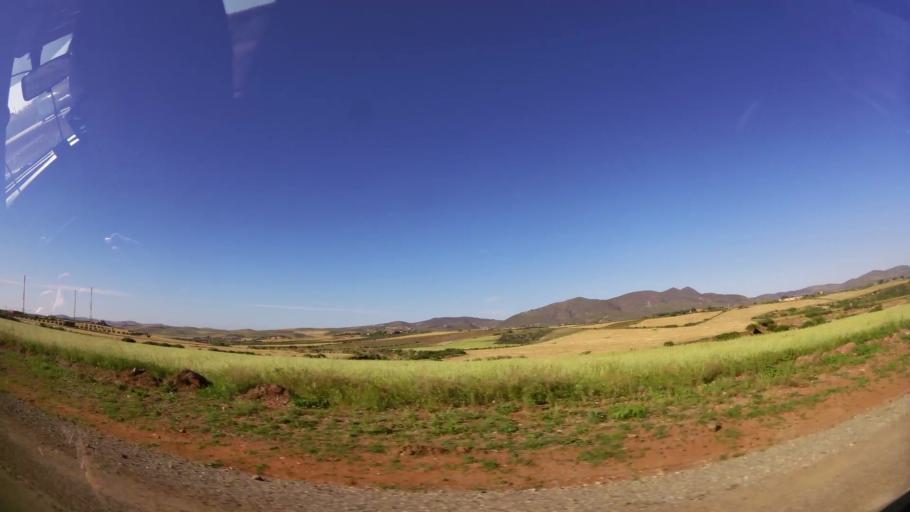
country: MA
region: Oriental
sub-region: Berkane-Taourirt
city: Ahfir
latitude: 34.9836
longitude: -2.1439
